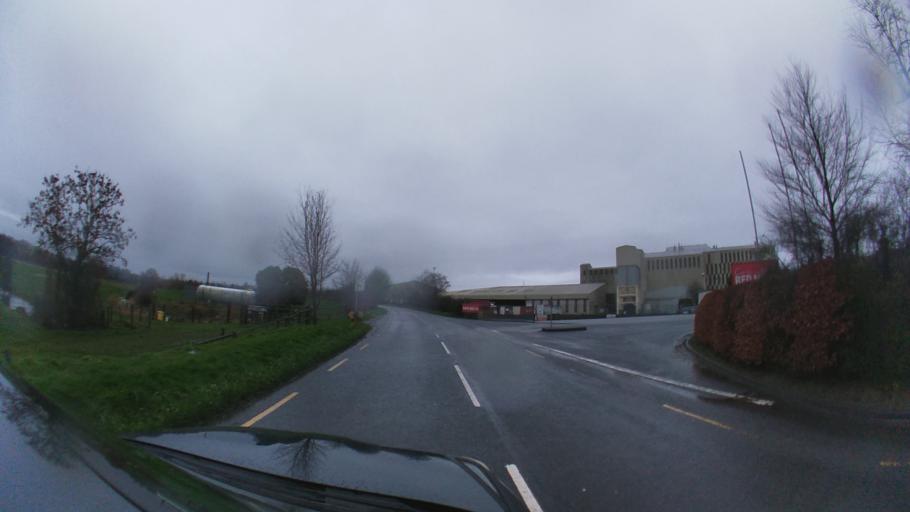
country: IE
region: Leinster
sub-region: County Carlow
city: Bagenalstown
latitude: 52.6362
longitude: -6.9939
